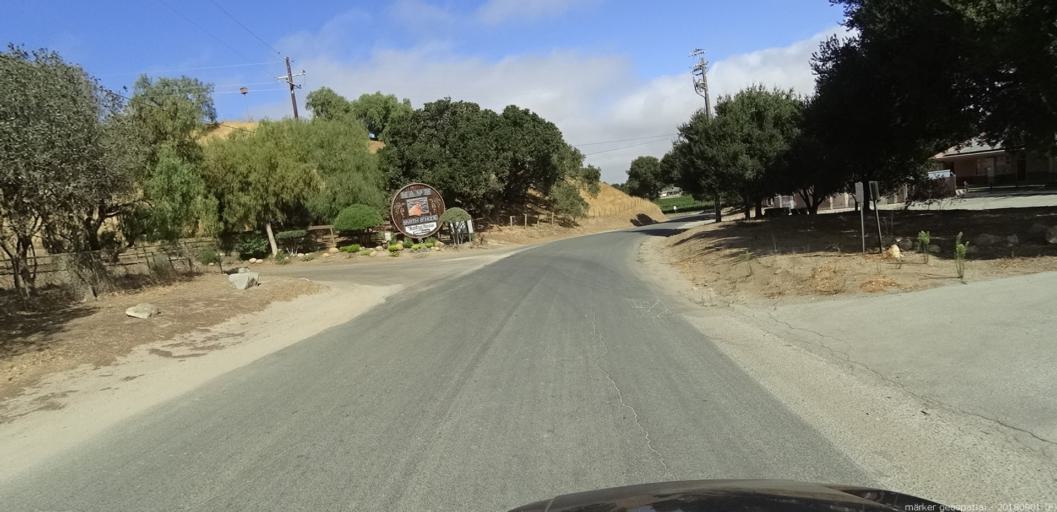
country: US
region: California
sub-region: Monterey County
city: Soledad
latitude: 36.3898
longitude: -121.3652
